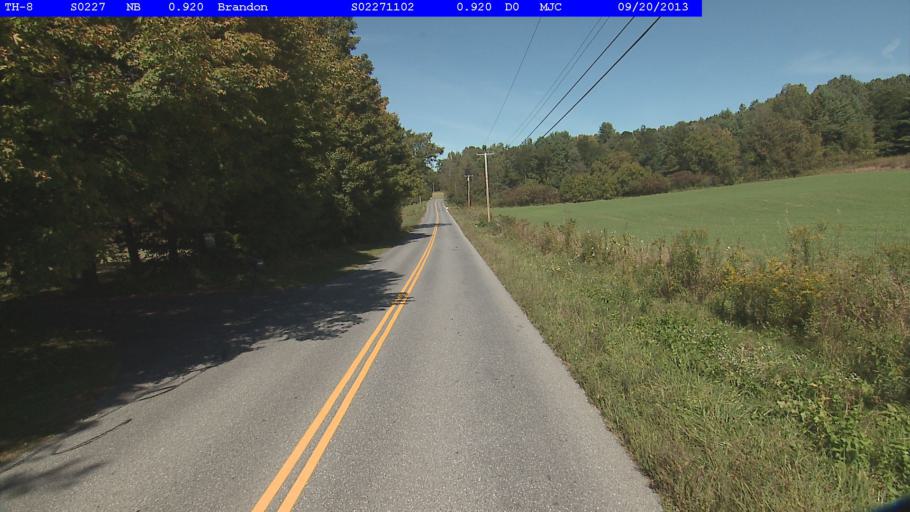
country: US
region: Vermont
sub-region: Rutland County
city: Brandon
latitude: 43.7876
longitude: -73.0536
